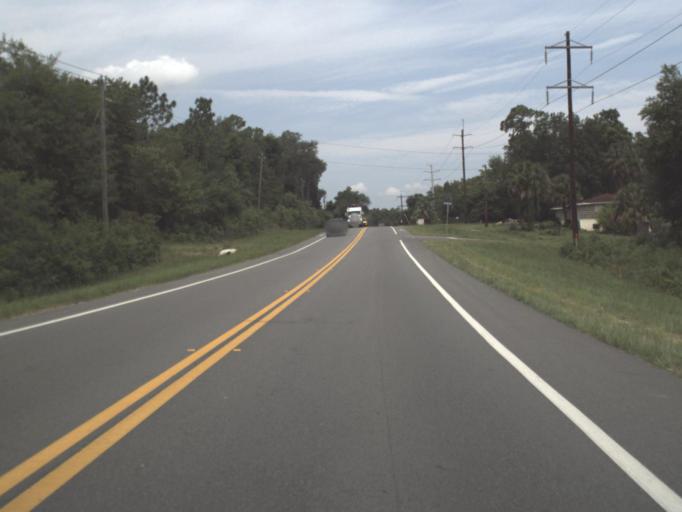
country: US
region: Florida
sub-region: Putnam County
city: Interlachen
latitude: 29.6237
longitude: -81.9412
